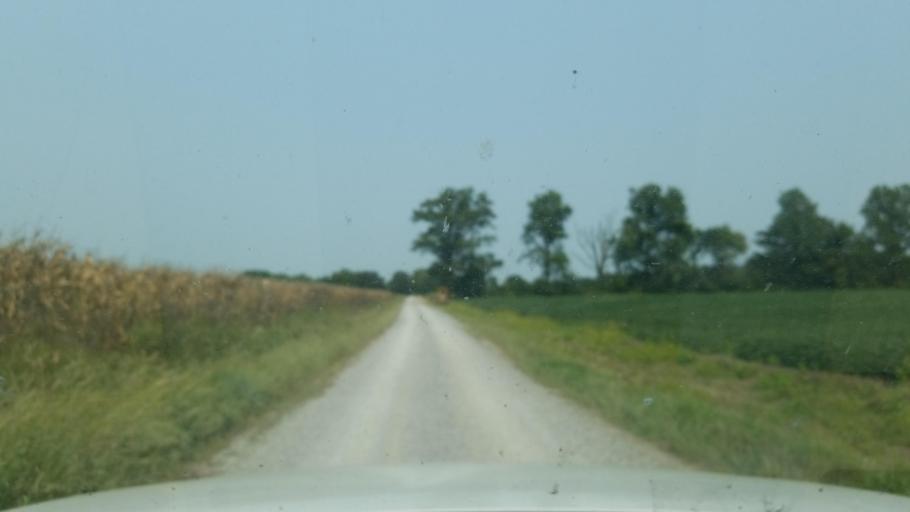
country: US
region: Illinois
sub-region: Saline County
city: Eldorado
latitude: 37.8184
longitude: -88.5166
